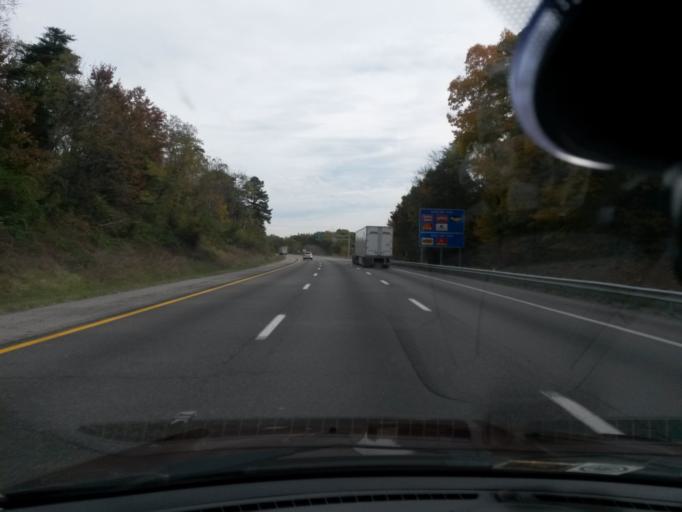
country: US
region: Virginia
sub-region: Botetourt County
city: Cloverdale
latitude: 37.3658
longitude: -79.9272
